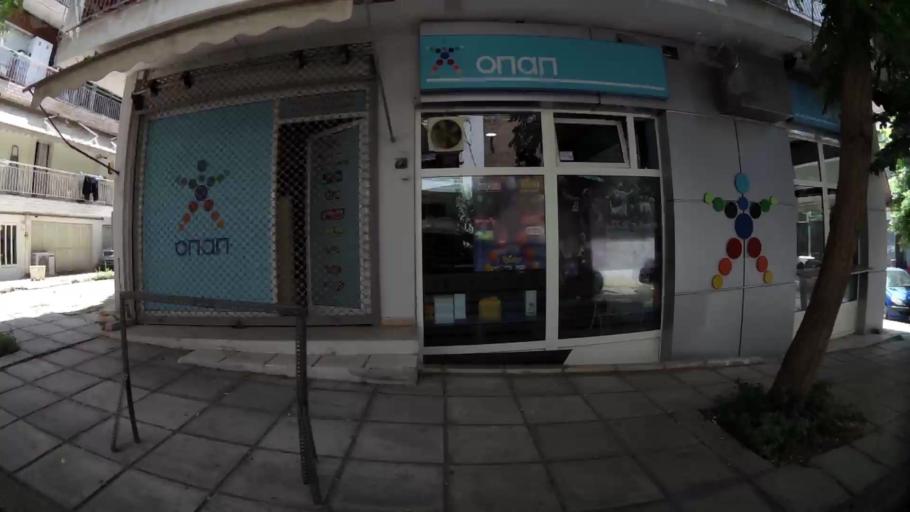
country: GR
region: Central Macedonia
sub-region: Nomos Thessalonikis
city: Triandria
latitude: 40.6135
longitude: 22.9754
